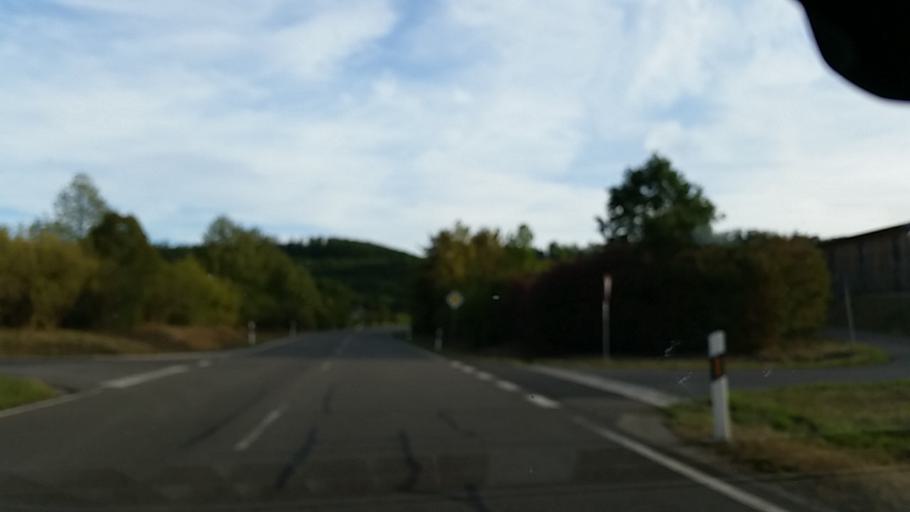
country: DE
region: Thuringia
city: Henneberg
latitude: 50.4934
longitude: 10.3512
